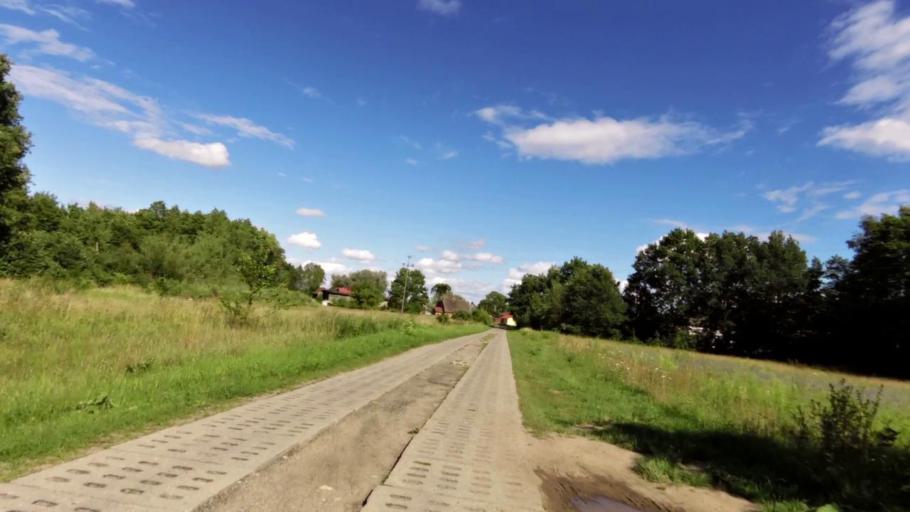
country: PL
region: West Pomeranian Voivodeship
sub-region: Powiat slawienski
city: Slawno
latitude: 54.4608
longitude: 16.7320
